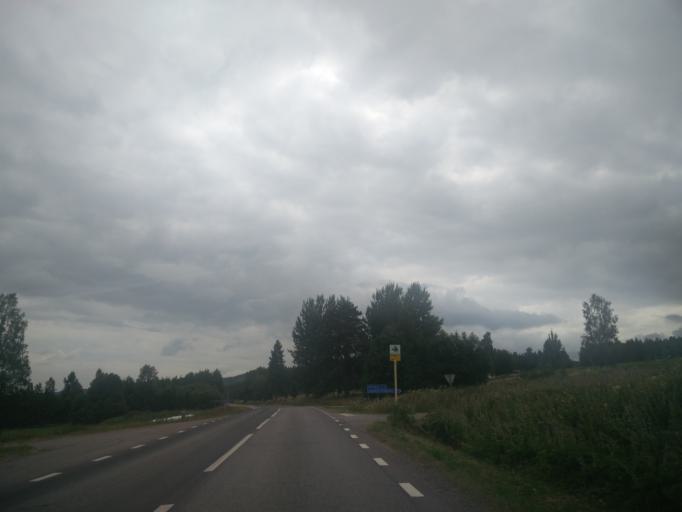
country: SE
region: Vaermland
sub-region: Torsby Kommun
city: Torsby
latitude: 59.9268
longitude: 12.8975
